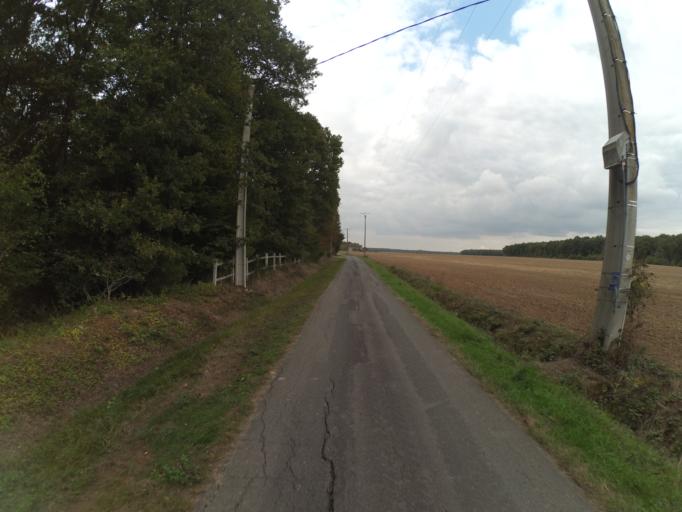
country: FR
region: Centre
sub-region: Departement d'Indre-et-Loire
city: Auzouer-en-Touraine
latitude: 47.5154
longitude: 0.9836
